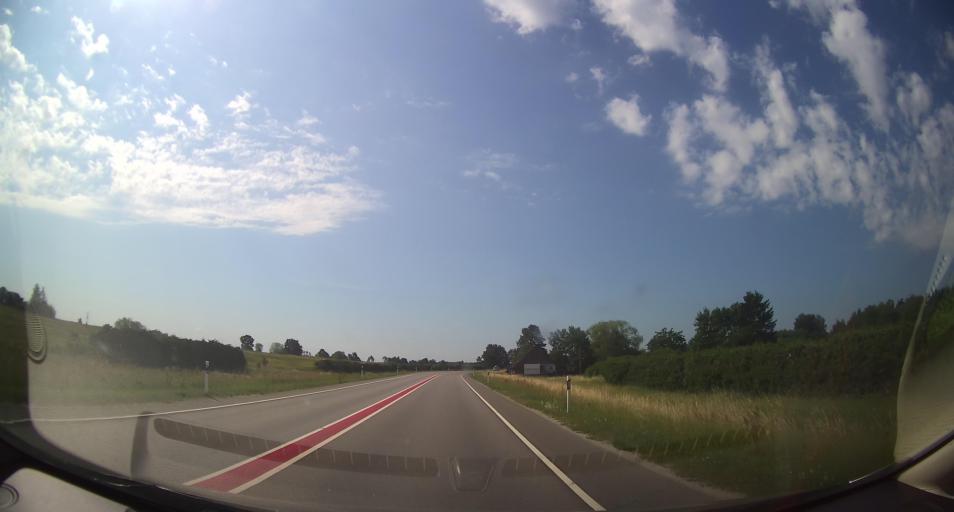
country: EE
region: Harju
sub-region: Saku vald
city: Saku
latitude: 59.3049
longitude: 24.7456
